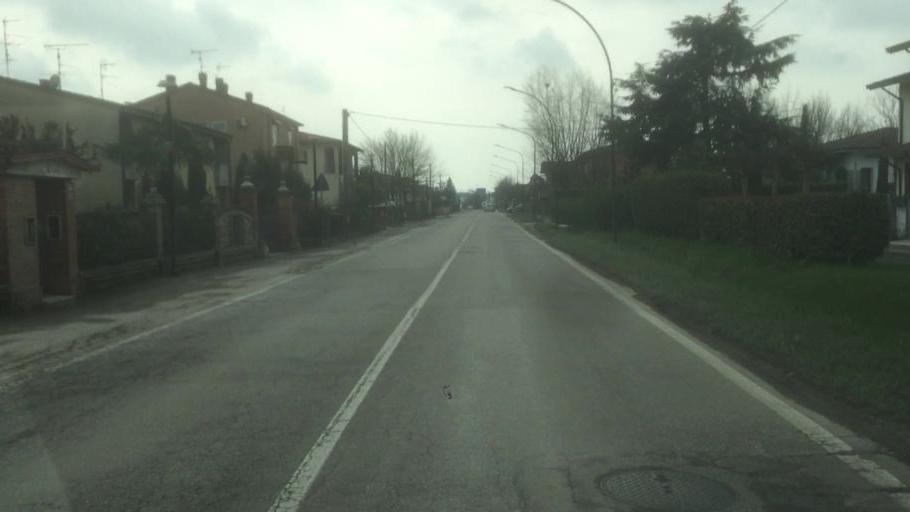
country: IT
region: Lombardy
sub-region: Provincia di Mantova
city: Casaloldo
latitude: 45.2583
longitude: 10.4755
